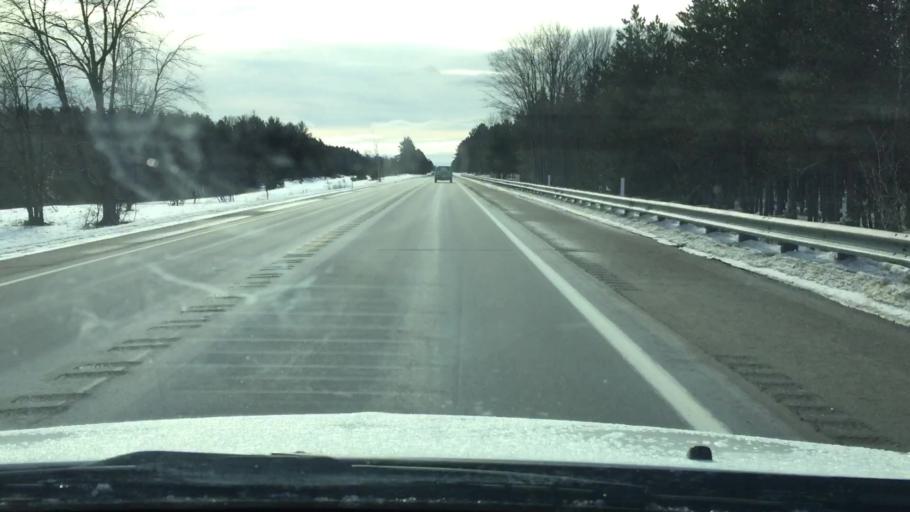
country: US
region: Michigan
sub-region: Kalkaska County
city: Kalkaska
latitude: 44.6908
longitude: -85.2155
